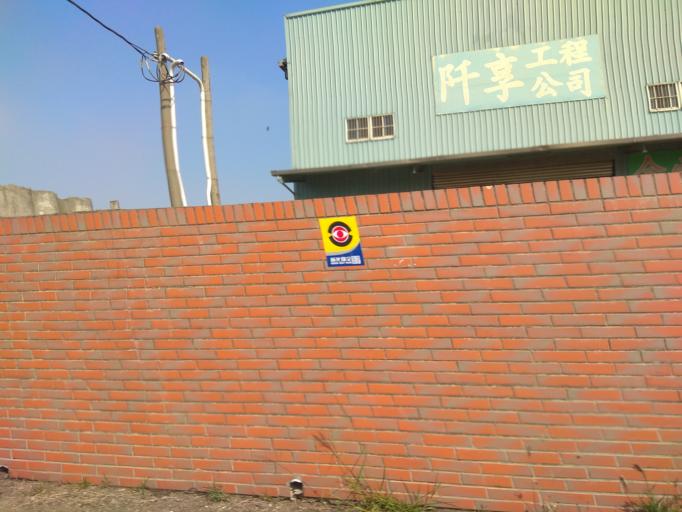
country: TW
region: Taiwan
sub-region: Hsinchu
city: Zhubei
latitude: 24.9952
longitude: 121.0649
